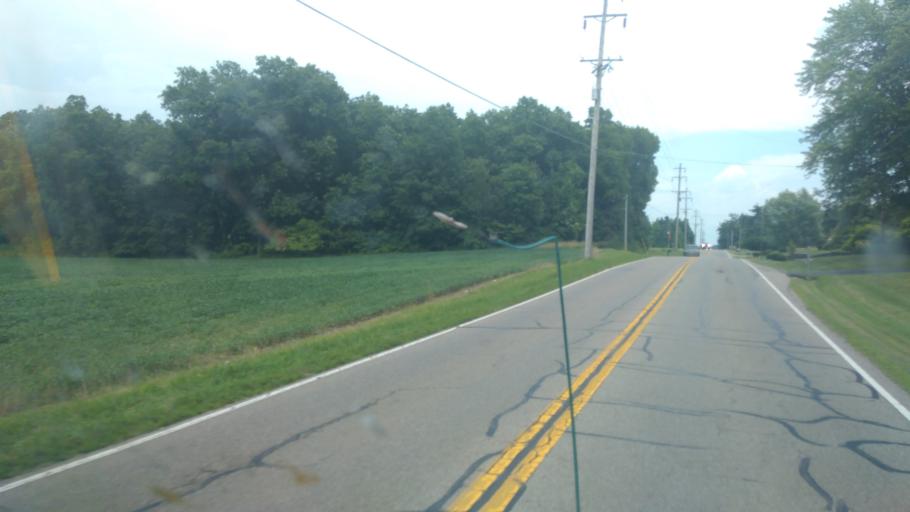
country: US
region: Ohio
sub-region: Fairfield County
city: Lancaster
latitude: 39.7687
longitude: -82.6123
